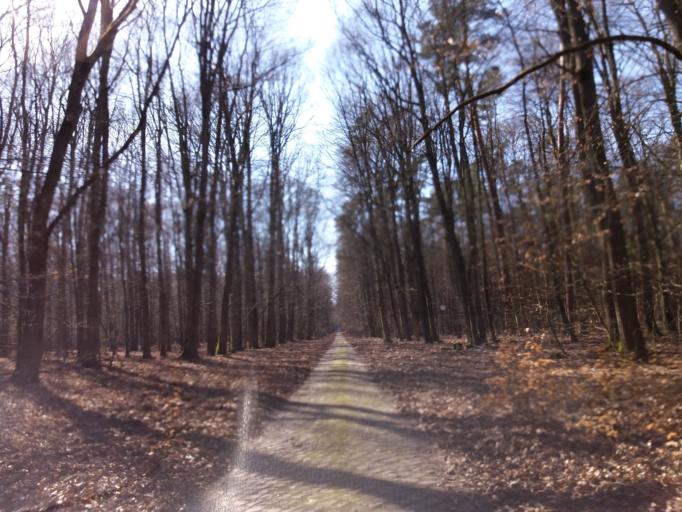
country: PL
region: West Pomeranian Voivodeship
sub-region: Powiat choszczenski
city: Drawno
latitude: 53.1019
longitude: 15.8632
